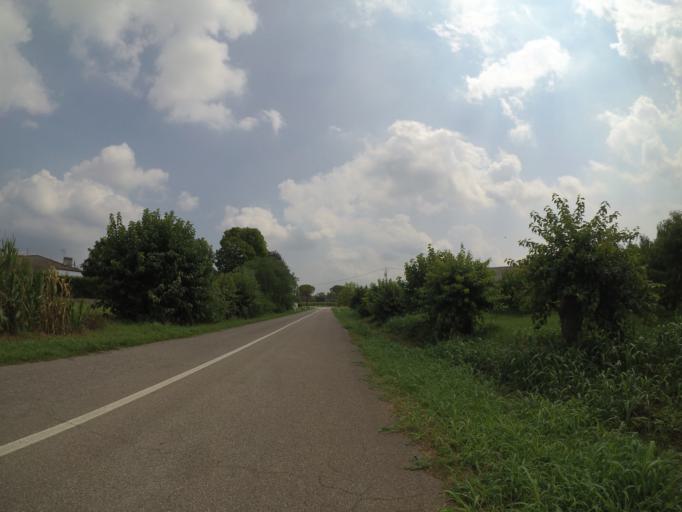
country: IT
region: Friuli Venezia Giulia
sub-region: Provincia di Udine
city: Sedegliano
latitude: 45.9956
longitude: 13.0197
